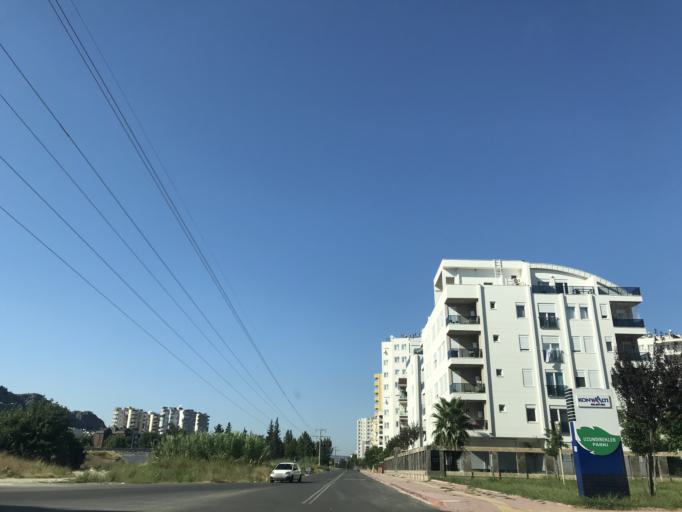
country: TR
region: Antalya
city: Cakirlar
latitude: 36.8541
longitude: 30.6066
